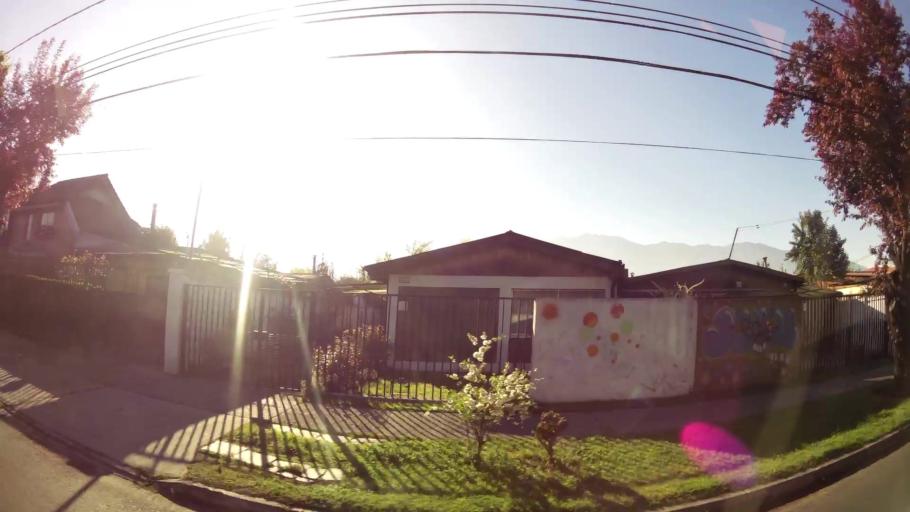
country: CL
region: Santiago Metropolitan
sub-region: Provincia de Santiago
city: Villa Presidente Frei, Nunoa, Santiago, Chile
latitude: -33.4575
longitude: -70.5644
